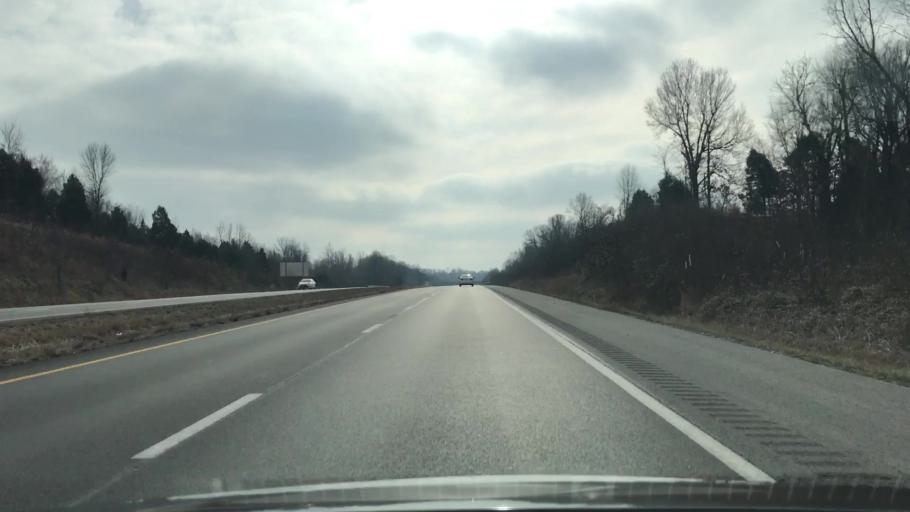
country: US
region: Kentucky
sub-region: Hopkins County
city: Madisonville
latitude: 37.4030
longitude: -87.4750
